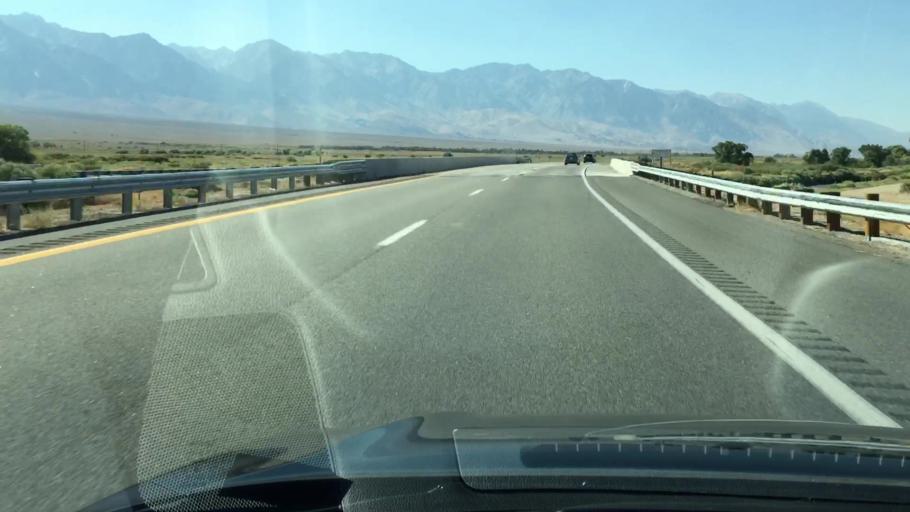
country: US
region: California
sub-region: Inyo County
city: Lone Pine
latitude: 36.7058
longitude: -118.1270
